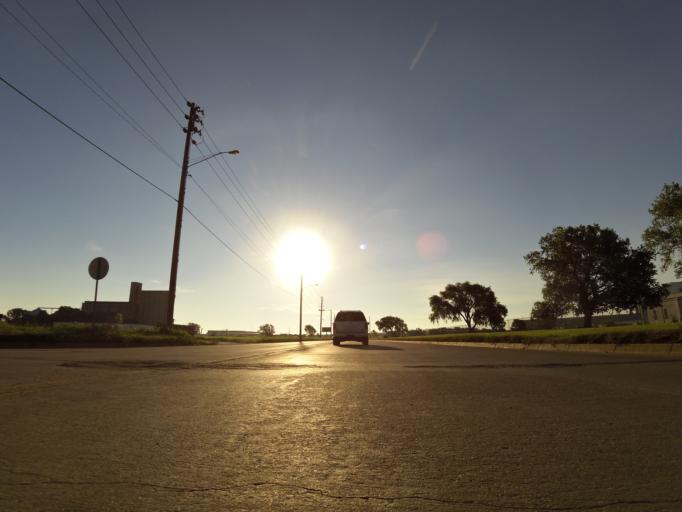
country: US
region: Kansas
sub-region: Sedgwick County
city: Wichita
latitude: 37.7375
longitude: -97.3308
